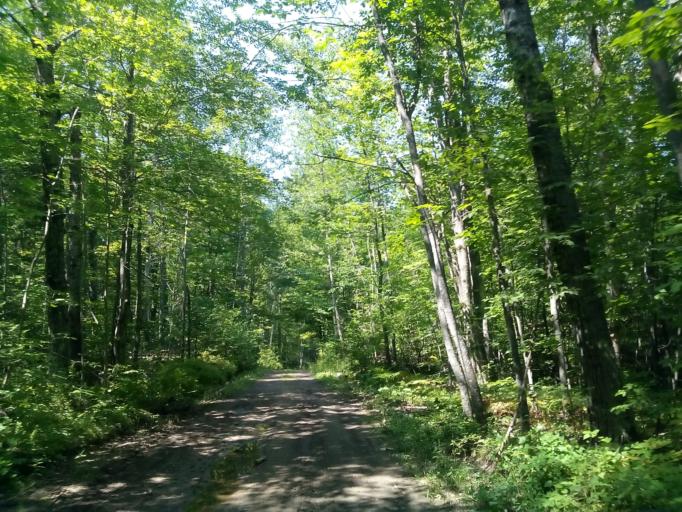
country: US
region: Wisconsin
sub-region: Forest County
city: Crandon
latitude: 45.3624
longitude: -88.5254
